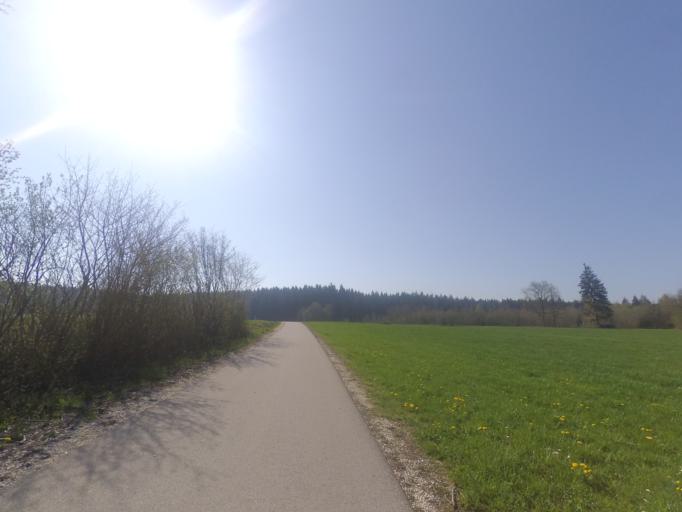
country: DE
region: Bavaria
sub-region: Swabia
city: Nersingen
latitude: 48.4067
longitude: 10.1602
